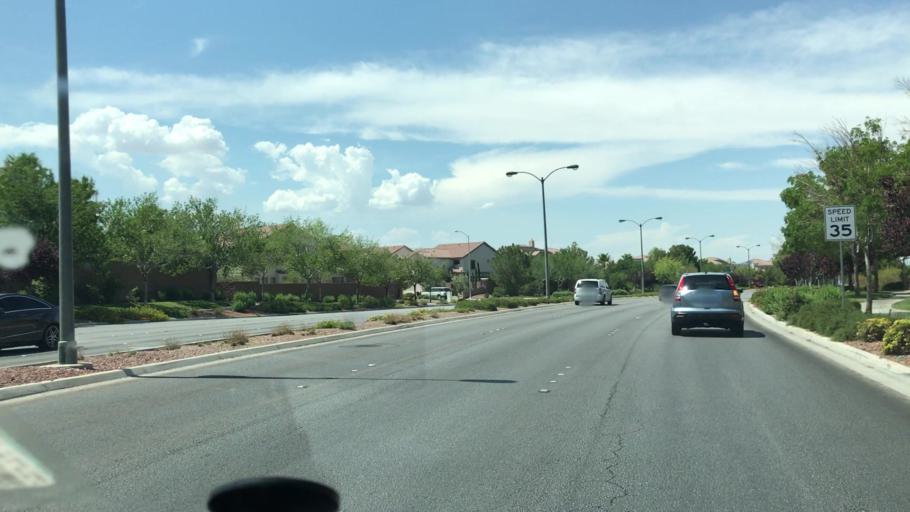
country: US
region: Nevada
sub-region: Clark County
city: Enterprise
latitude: 35.9947
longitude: -115.2069
